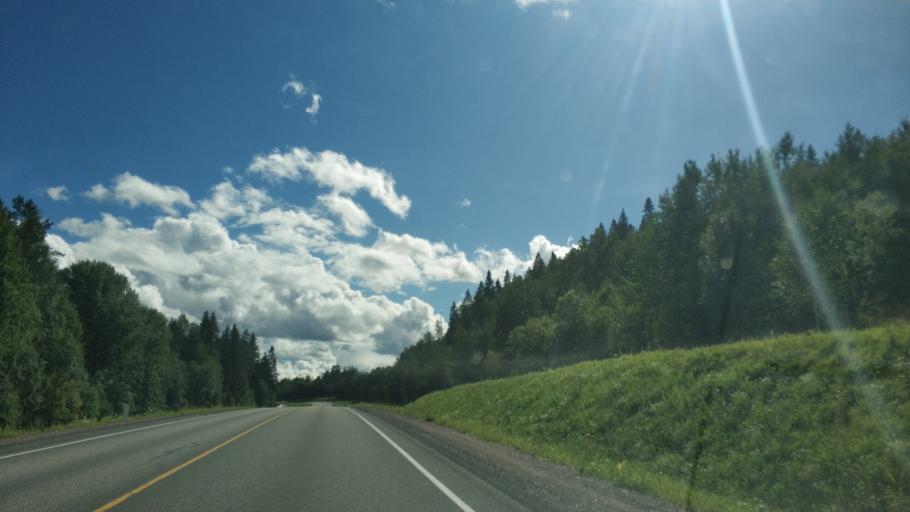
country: RU
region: Republic of Karelia
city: Ruskeala
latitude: 61.8996
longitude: 30.6358
